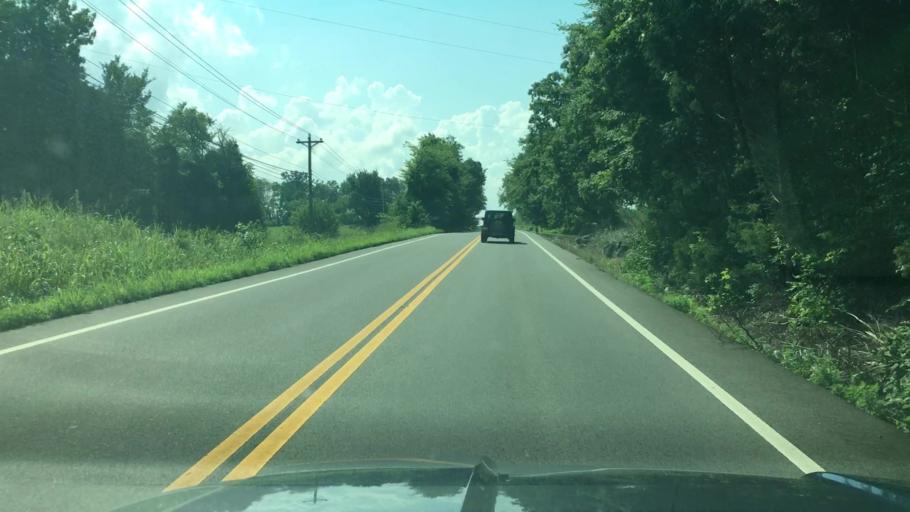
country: US
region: Tennessee
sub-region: Williamson County
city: Nolensville
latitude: 35.8818
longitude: -86.7465
